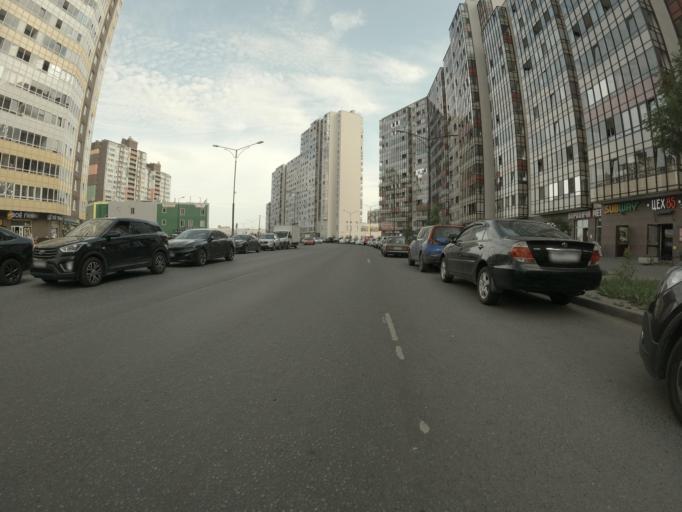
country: RU
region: Leningrad
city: Rybatskoye
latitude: 59.8995
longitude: 30.5117
